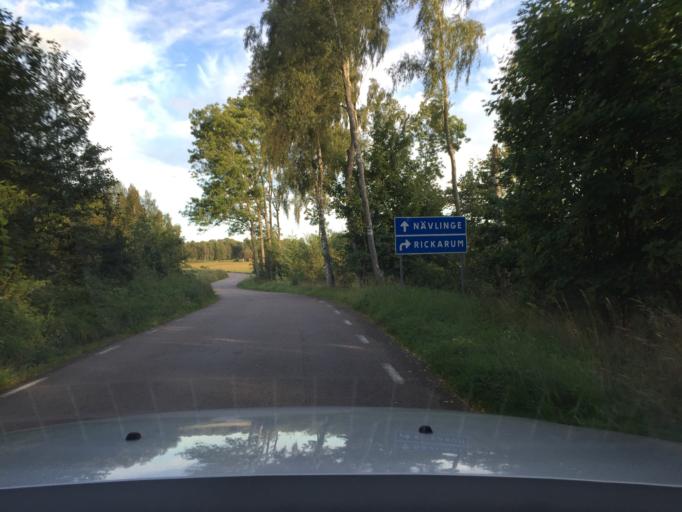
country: SE
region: Skane
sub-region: Hassleholms Kommun
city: Sosdala
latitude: 56.0352
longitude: 13.7433
